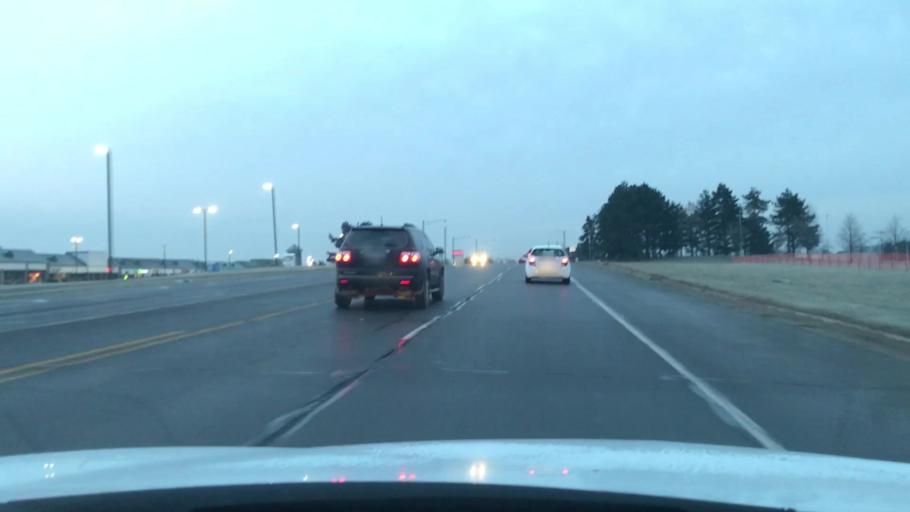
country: US
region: Michigan
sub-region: Oakland County
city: Sylvan Lake
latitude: 42.6465
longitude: -83.3264
